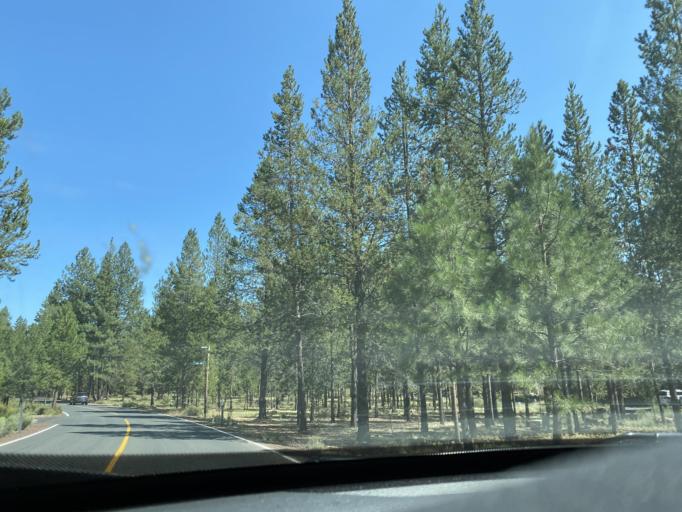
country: US
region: Oregon
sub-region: Deschutes County
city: Sunriver
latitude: 43.8887
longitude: -121.4320
